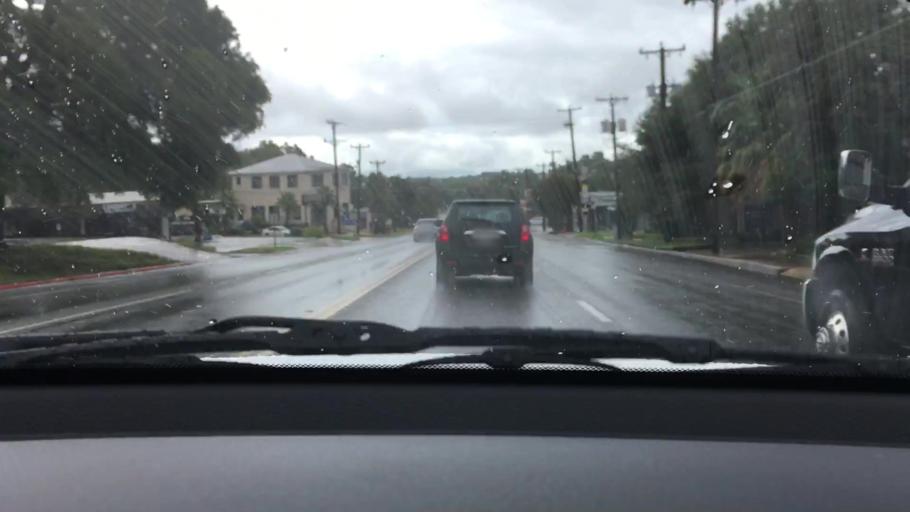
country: US
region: Texas
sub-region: Bexar County
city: Alamo Heights
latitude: 29.4828
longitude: -98.4661
